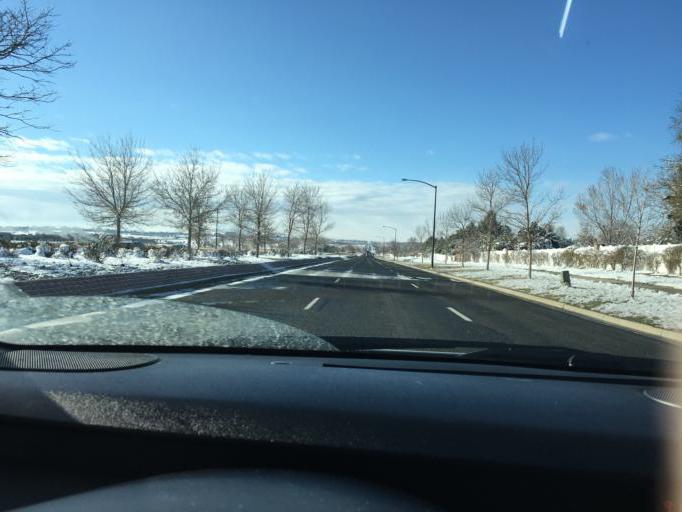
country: US
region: Colorado
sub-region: Adams County
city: Northglenn
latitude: 39.9507
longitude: -104.9969
